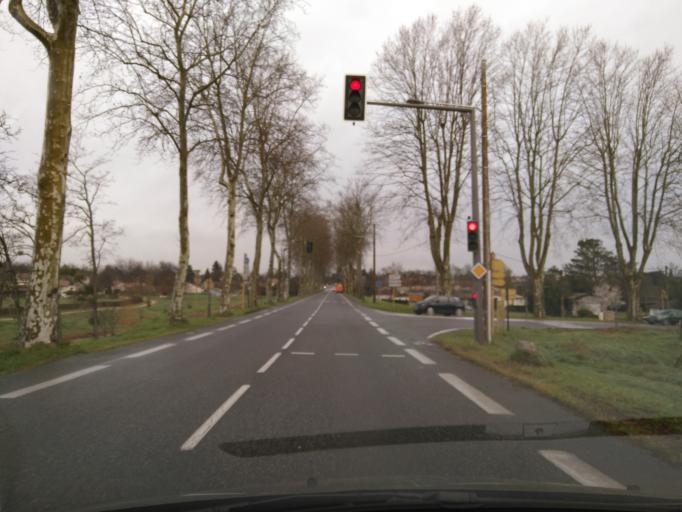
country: FR
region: Midi-Pyrenees
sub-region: Departement de la Haute-Garonne
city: Carbonne
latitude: 43.2907
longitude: 1.2165
